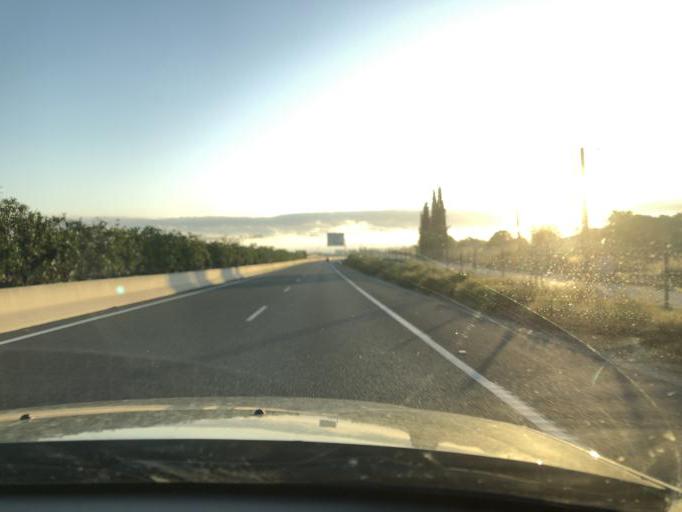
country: ES
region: Balearic Islands
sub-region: Illes Balears
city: Montuiri
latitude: 39.5621
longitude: 2.9654
